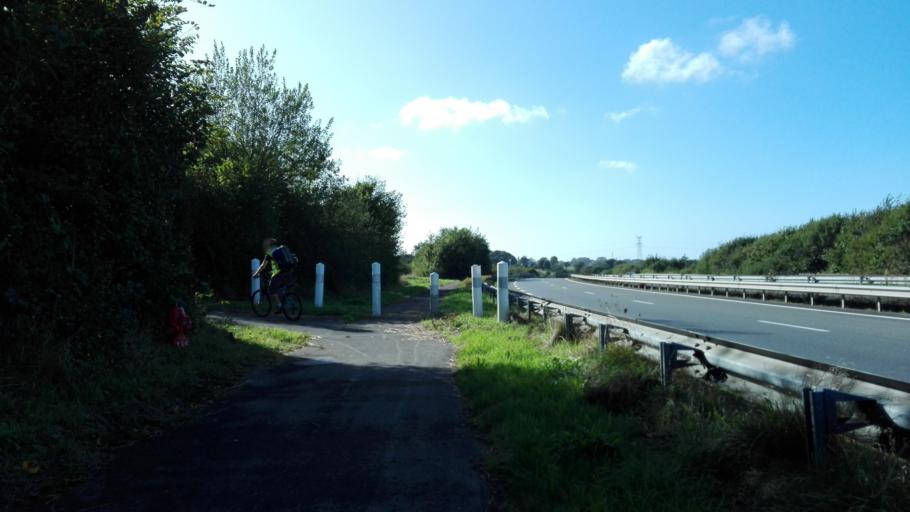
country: FR
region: Nord-Pas-de-Calais
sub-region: Departement du Pas-de-Calais
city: Baincthun
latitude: 50.7303
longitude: 1.6652
